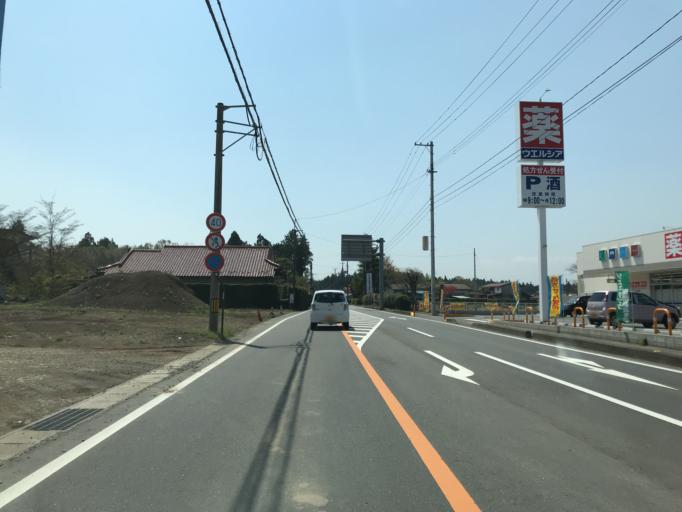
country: JP
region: Fukushima
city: Ishikawa
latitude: 37.1444
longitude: 140.3492
